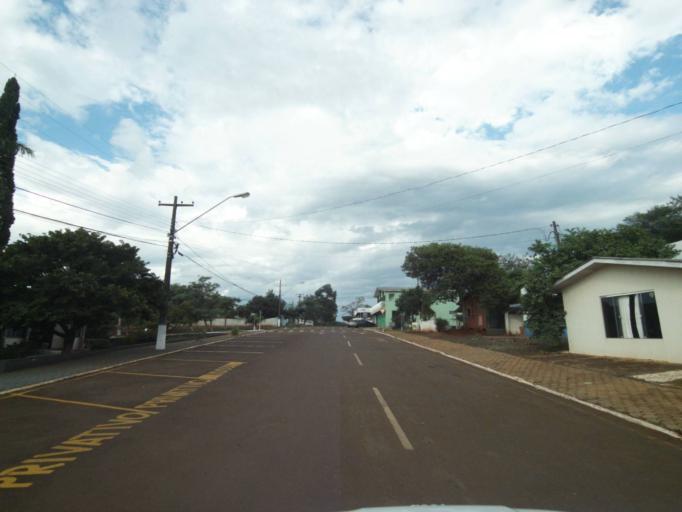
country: BR
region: Parana
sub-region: Laranjeiras Do Sul
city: Laranjeiras do Sul
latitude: -25.4909
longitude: -52.5256
